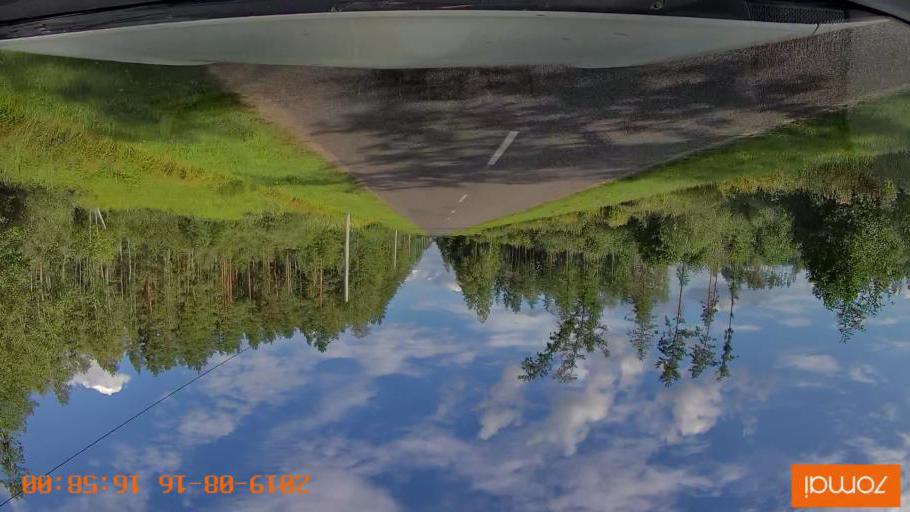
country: BY
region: Mogilev
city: Hlusha
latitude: 53.2635
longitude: 28.8294
